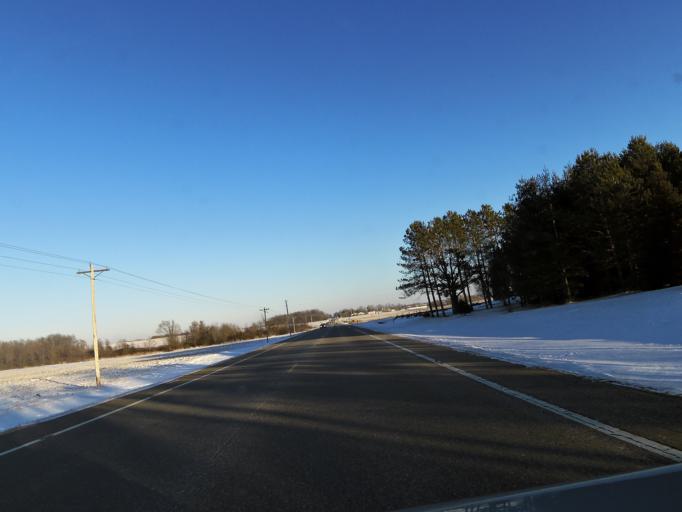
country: US
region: Minnesota
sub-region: Rice County
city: Northfield
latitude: 44.5437
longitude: -93.2126
